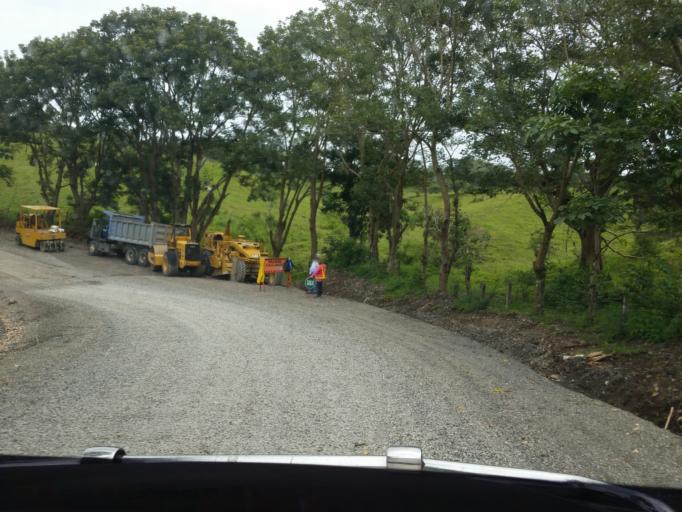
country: NI
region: Jinotega
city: Jinotega
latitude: 13.1751
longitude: -85.9175
